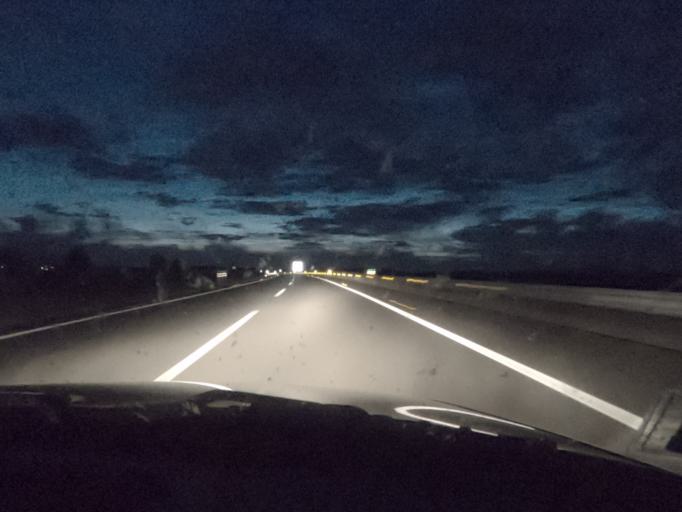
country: ES
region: Extremadura
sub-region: Provincia de Caceres
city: Morcillo
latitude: 39.9890
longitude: -6.4360
